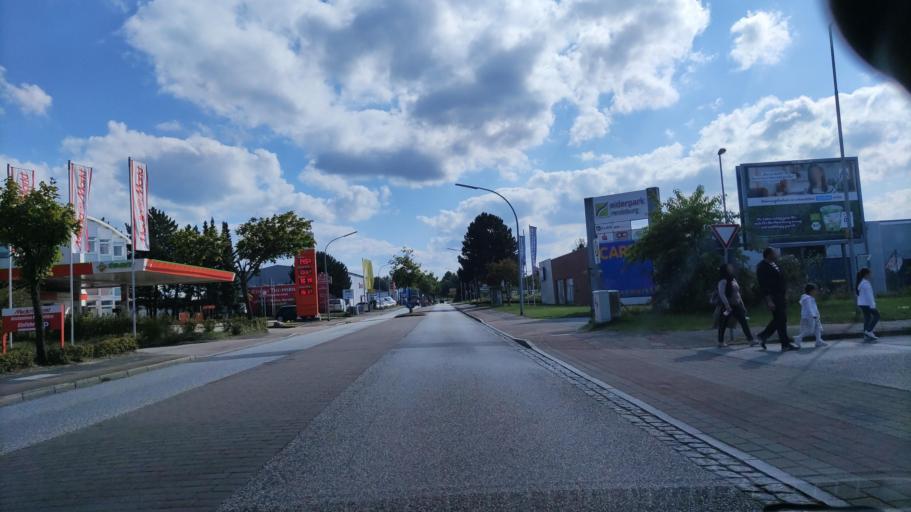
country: DE
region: Schleswig-Holstein
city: Fockbek
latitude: 54.3207
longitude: 9.6267
